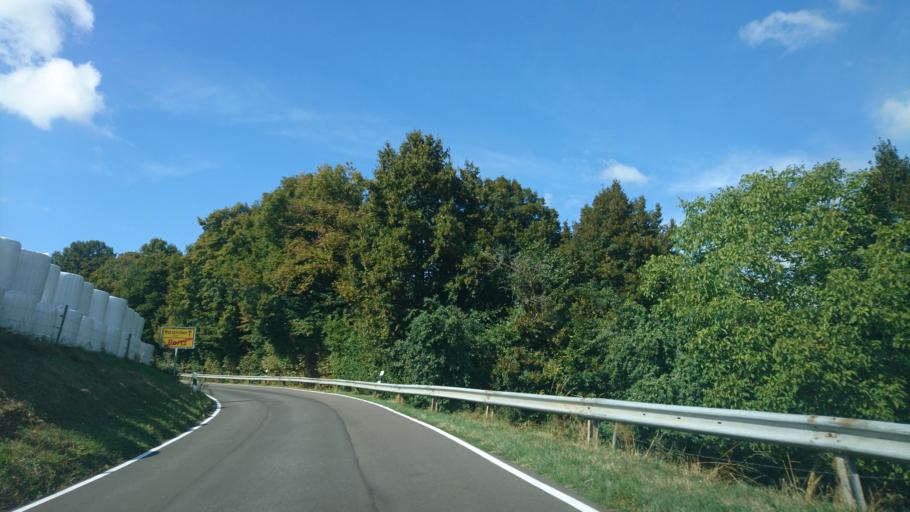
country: DE
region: Rheinland-Pfalz
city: Merzkirchen
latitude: 49.5791
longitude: 6.4889
